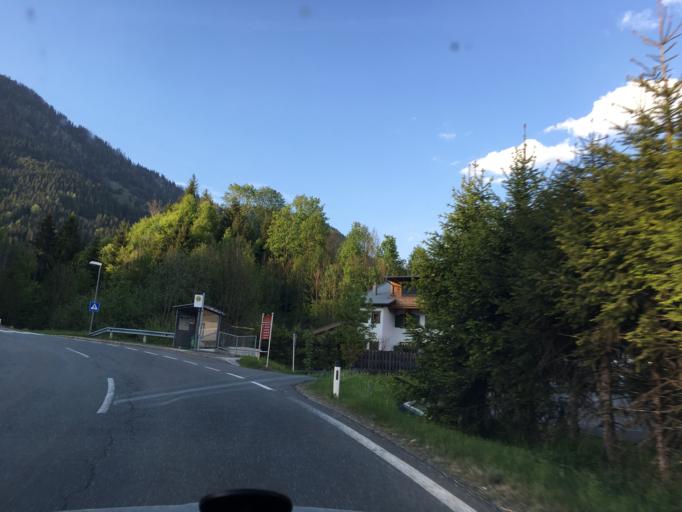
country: AT
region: Tyrol
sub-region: Politischer Bezirk Kitzbuhel
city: Fieberbrunn
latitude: 47.4936
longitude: 12.5434
